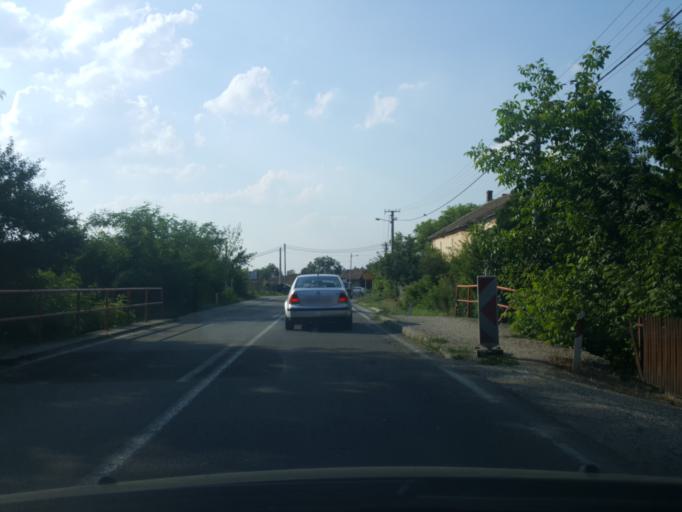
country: RS
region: Central Serbia
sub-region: Belgrade
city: Mladenovac
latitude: 44.4754
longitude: 20.6648
